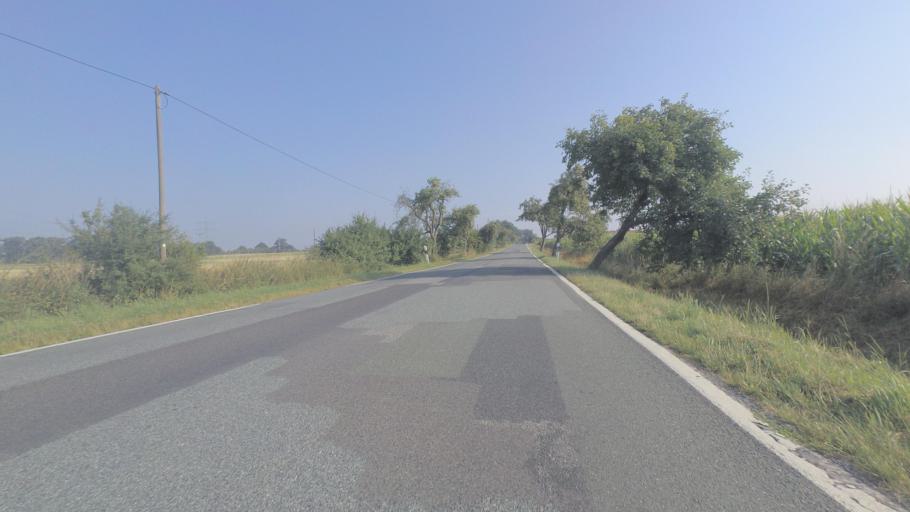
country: DE
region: Mecklenburg-Vorpommern
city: Malchow
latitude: 53.3715
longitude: 12.3858
